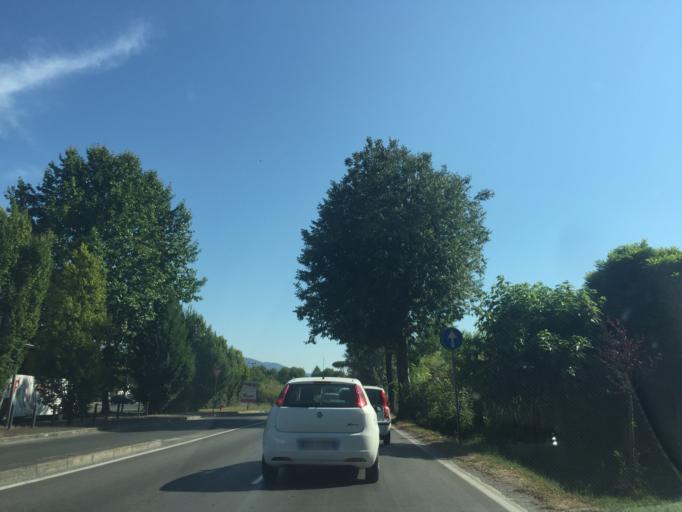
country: IT
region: Tuscany
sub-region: Provincia di Lucca
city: Lucca
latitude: 43.8477
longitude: 10.4948
